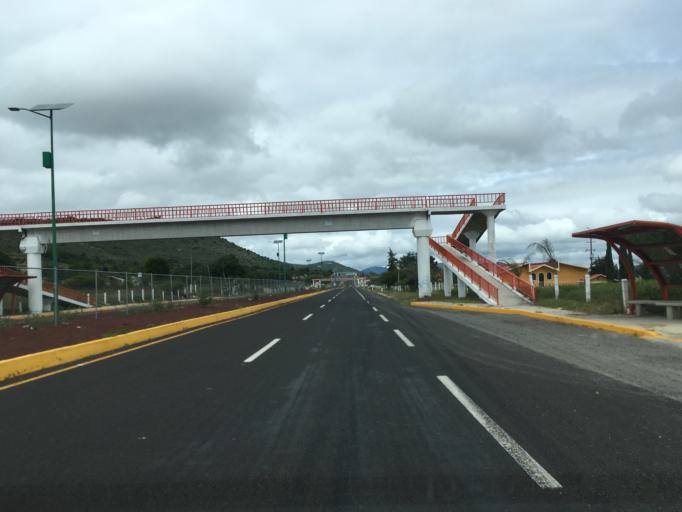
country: MX
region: Hidalgo
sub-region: Atotonilco el Grande
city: La Estancia
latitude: 20.3263
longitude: -98.6978
